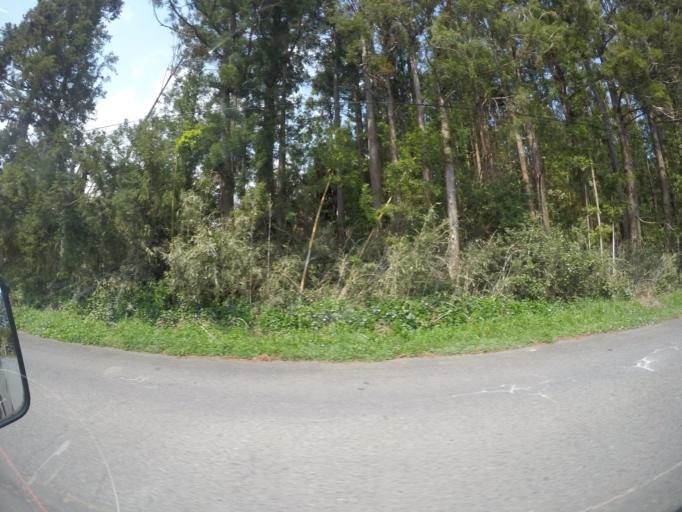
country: JP
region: Chiba
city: Omigawa
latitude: 35.8677
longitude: 140.5665
